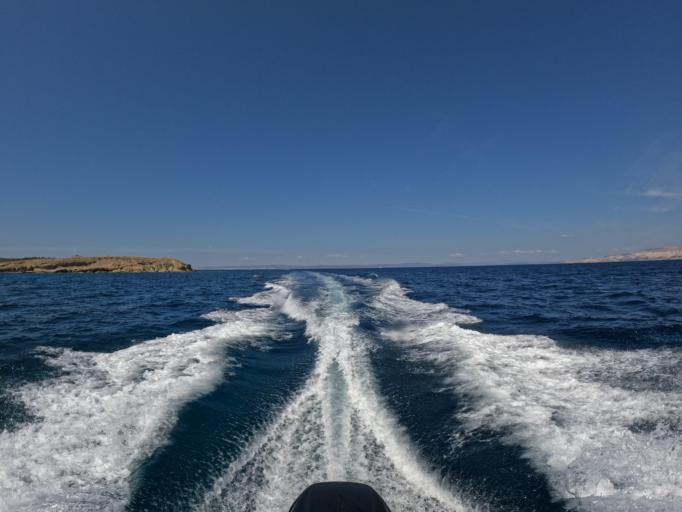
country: HR
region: Primorsko-Goranska
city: Lopar
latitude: 44.8545
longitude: 14.7309
